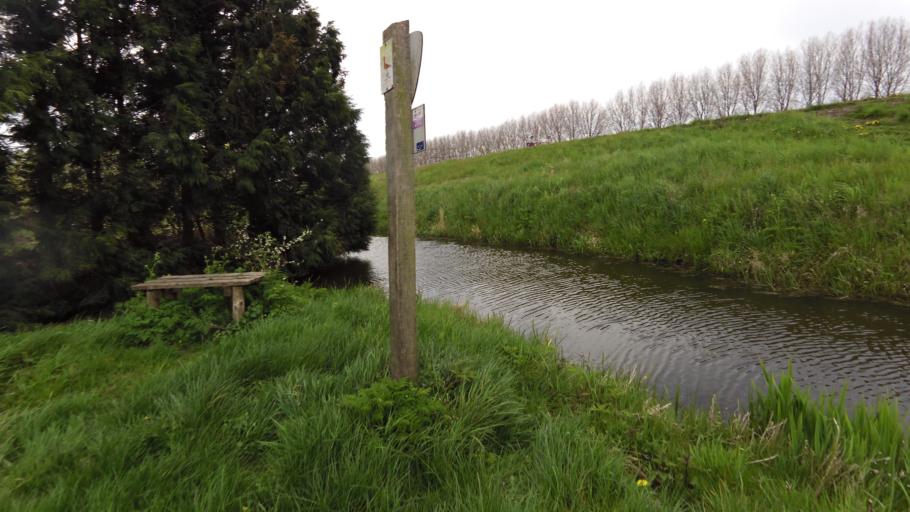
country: NL
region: Utrecht
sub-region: Stichtse Vecht
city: Vreeland
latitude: 52.2414
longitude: 5.0119
